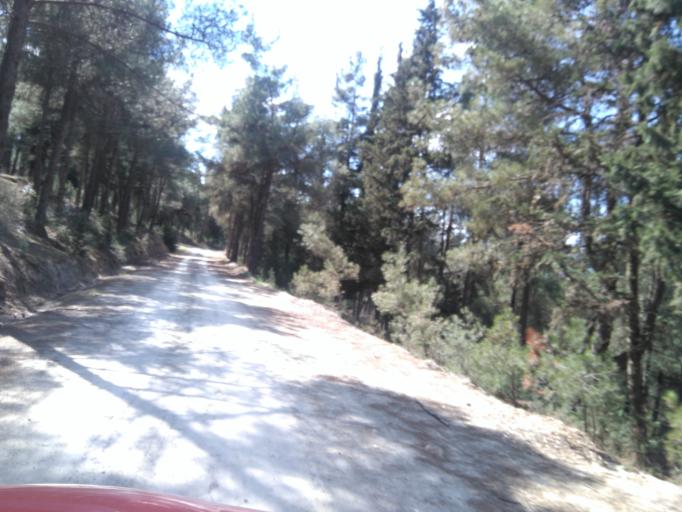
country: GR
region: Central Macedonia
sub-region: Nomos Thessalonikis
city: Pefka
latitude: 40.6480
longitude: 22.9791
